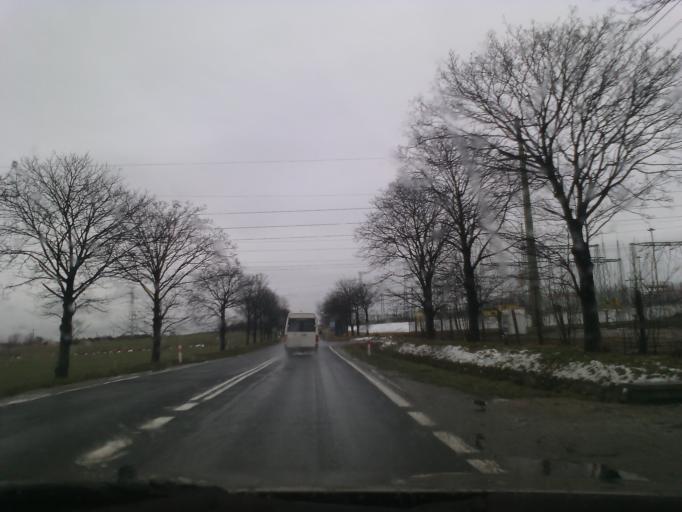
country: PL
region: Lower Silesian Voivodeship
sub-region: Powiat swidnicki
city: Swiebodzice
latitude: 50.8553
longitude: 16.3531
